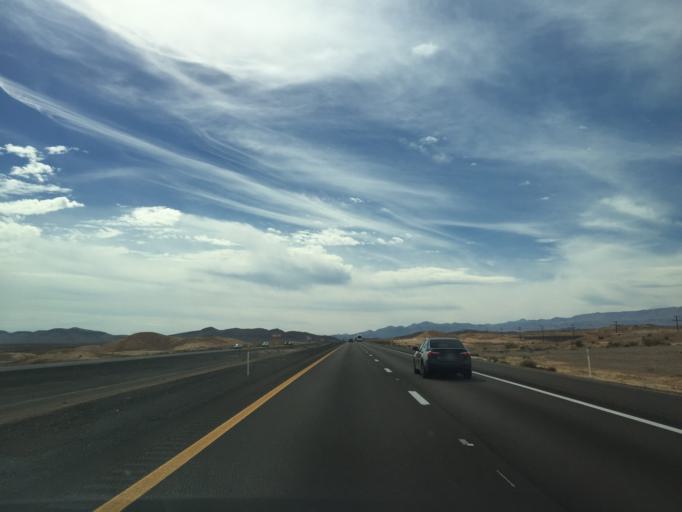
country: US
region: Nevada
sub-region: Clark County
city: Moapa Town
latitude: 36.4960
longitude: -114.7742
